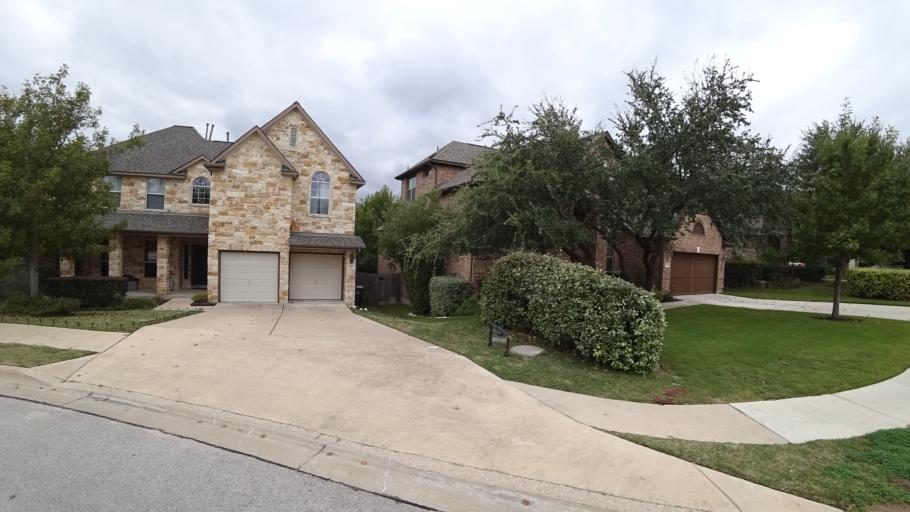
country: US
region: Texas
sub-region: Travis County
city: Bee Cave
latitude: 30.3458
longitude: -97.9118
